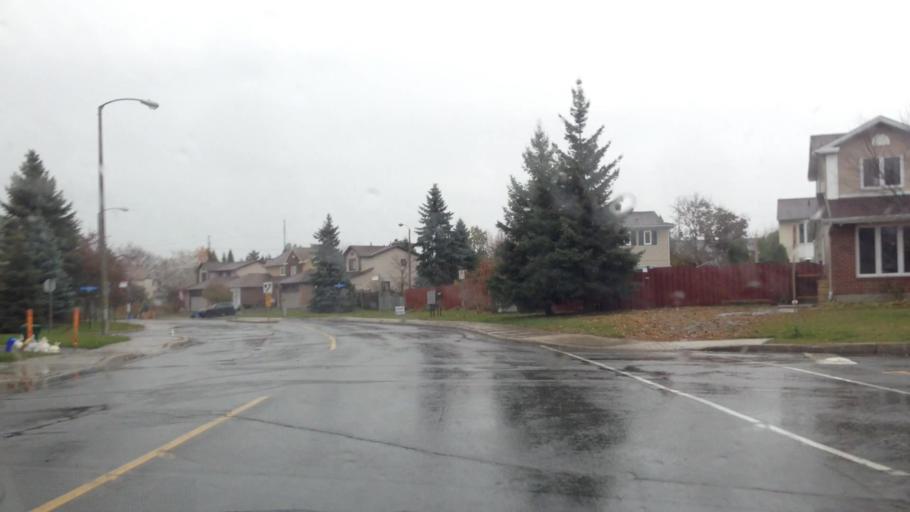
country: CA
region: Ontario
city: Clarence-Rockland
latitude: 45.4644
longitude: -75.4858
